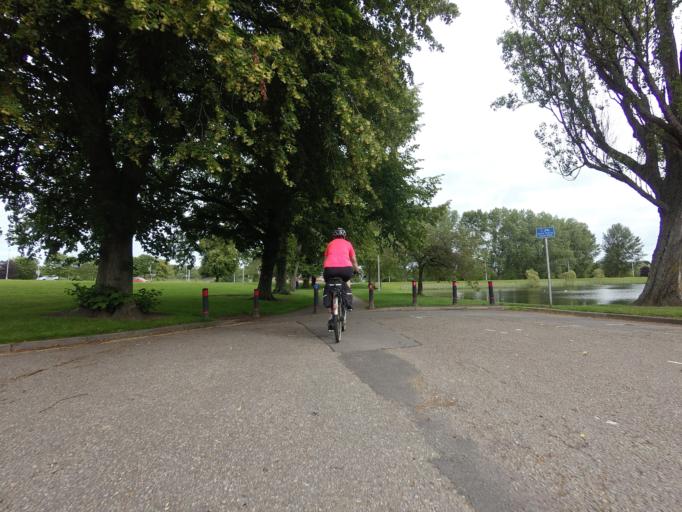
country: GB
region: Scotland
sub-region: Moray
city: Elgin
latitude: 57.6515
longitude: -3.3144
